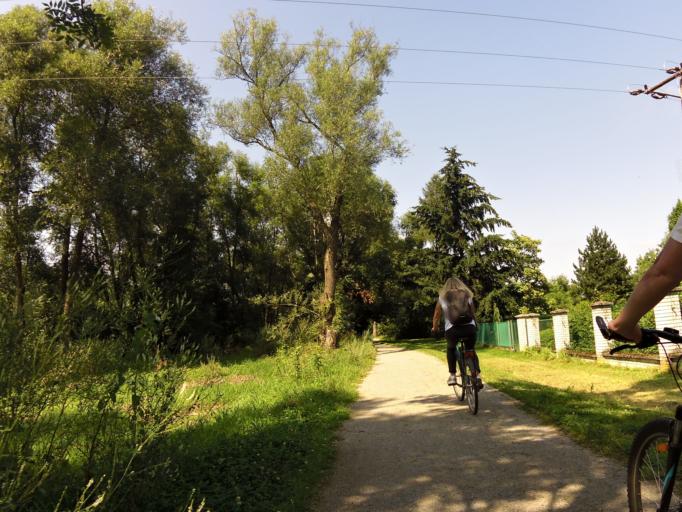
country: PL
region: Silesian Voivodeship
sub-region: Powiat zywiecki
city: Wegierska Gorka
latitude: 49.6134
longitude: 19.1269
